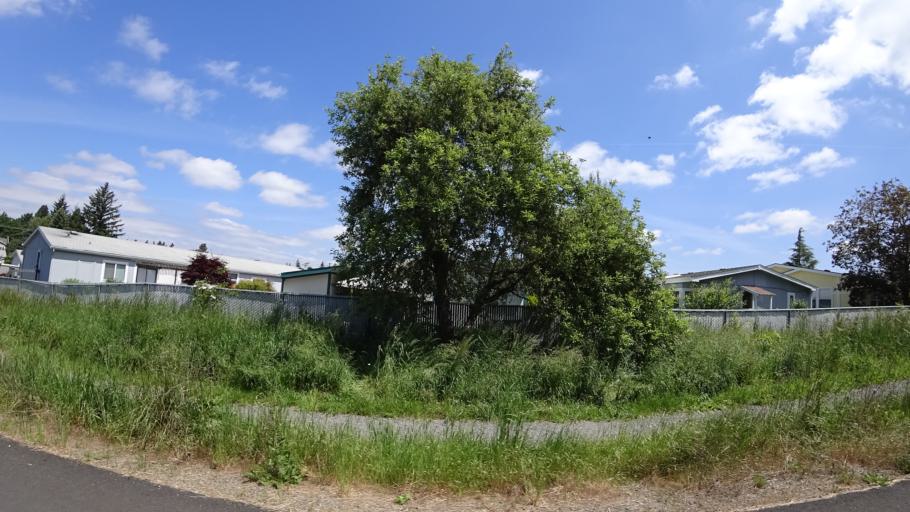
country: US
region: Oregon
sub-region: Clackamas County
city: Happy Valley
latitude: 45.4935
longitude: -122.4965
